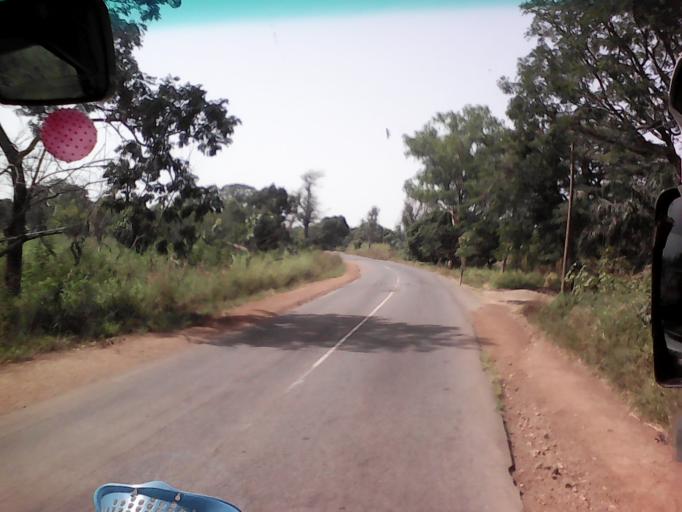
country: TG
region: Centrale
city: Sotouboua
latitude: 8.6969
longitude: 1.0247
